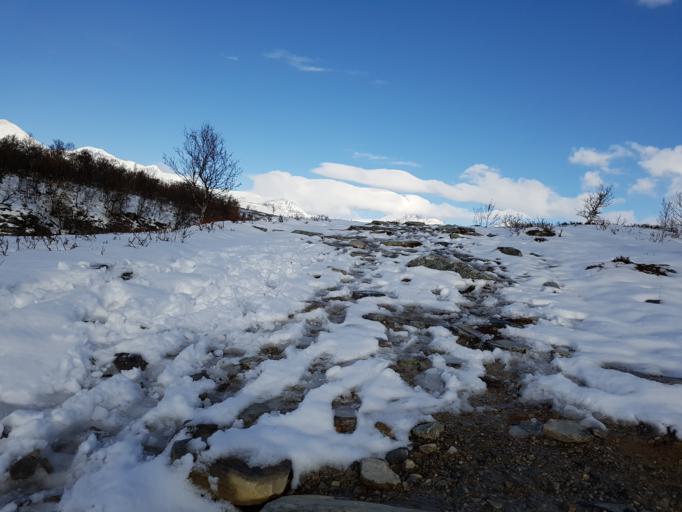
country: NO
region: Oppland
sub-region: Sel
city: Otta
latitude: 61.8288
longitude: 9.6963
